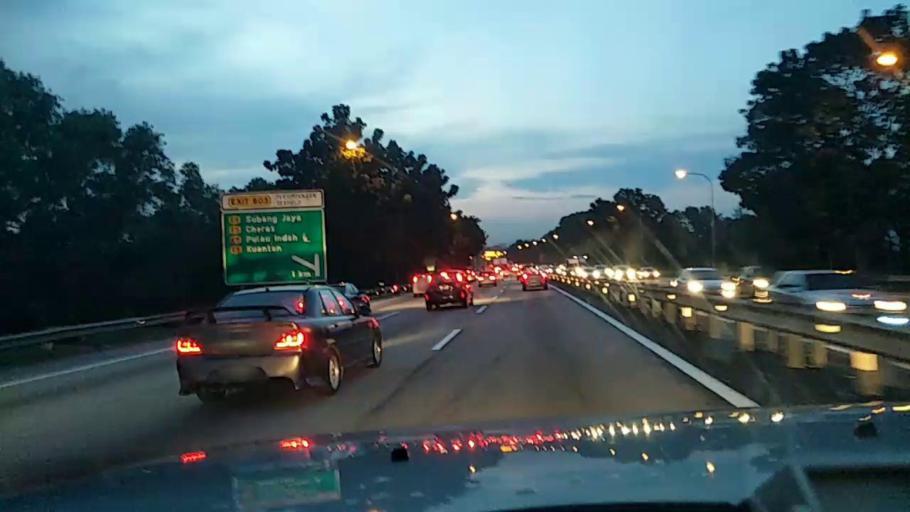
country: MY
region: Selangor
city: Subang Jaya
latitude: 3.0374
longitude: 101.5726
